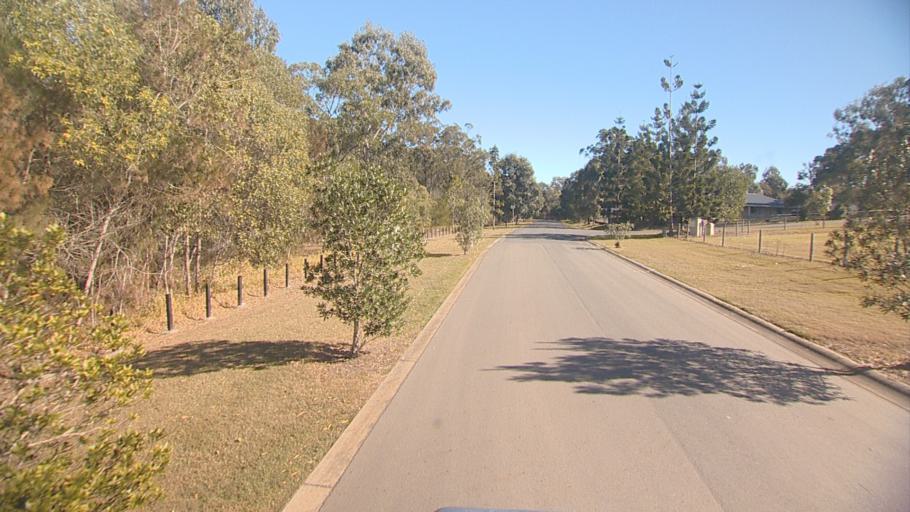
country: AU
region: Queensland
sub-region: Logan
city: North Maclean
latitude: -27.7512
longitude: 152.9666
